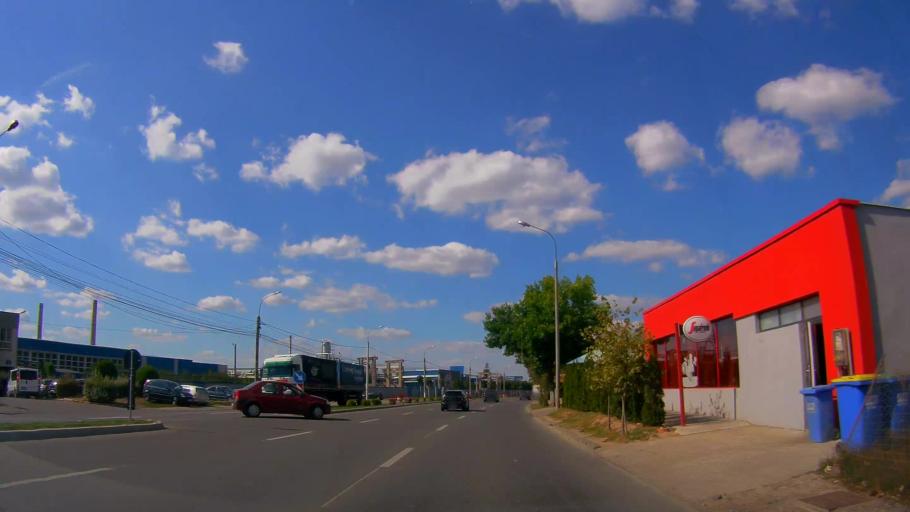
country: RO
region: Salaj
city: Zalau
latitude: 47.2061
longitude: 23.0473
